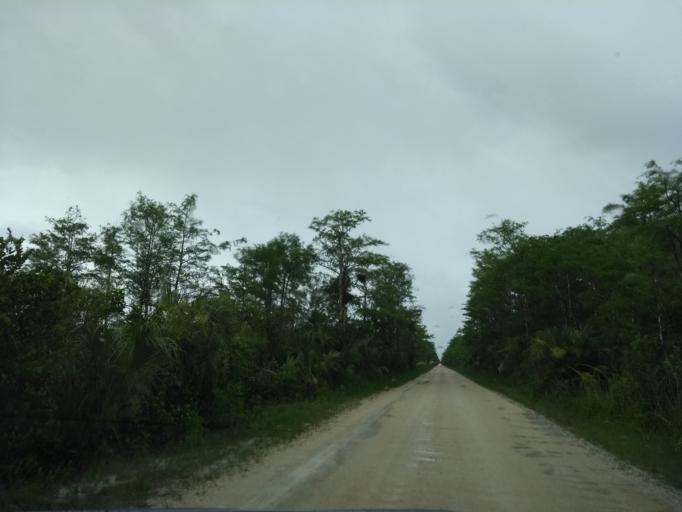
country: US
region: Florida
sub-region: Miami-Dade County
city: The Hammocks
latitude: 25.7602
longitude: -81.0239
